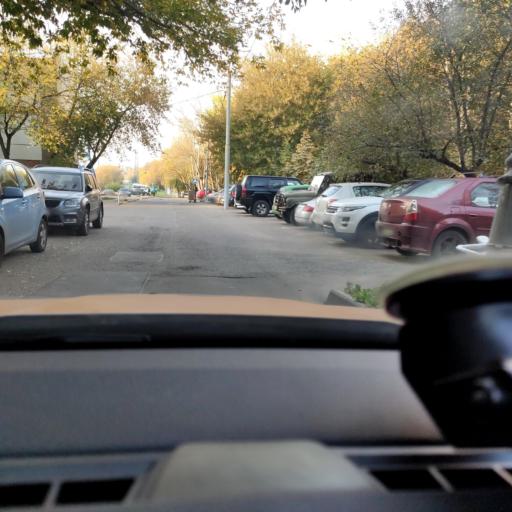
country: RU
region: Moscow
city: Kotlovka
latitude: 55.6761
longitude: 37.6065
